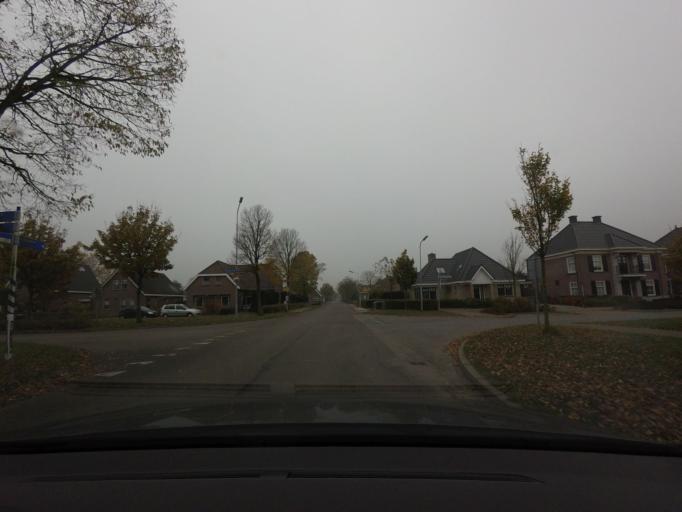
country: NL
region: North Holland
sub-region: Gemeente Schagen
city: Harenkarspel
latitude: 52.7338
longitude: 4.7564
